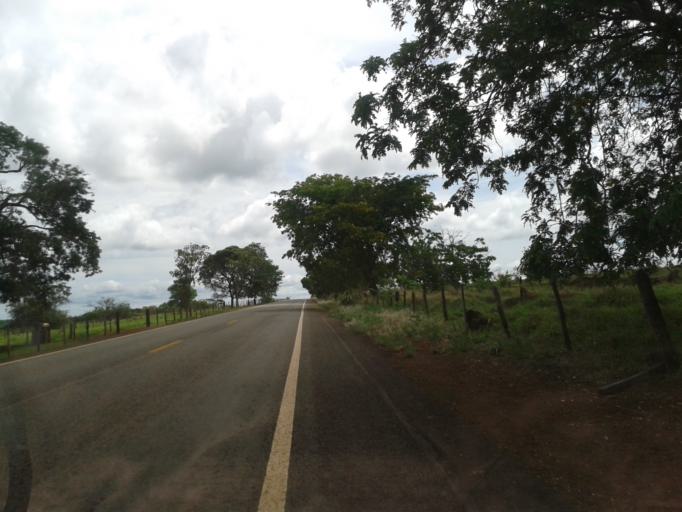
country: BR
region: Goias
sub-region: Buriti Alegre
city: Buriti Alegre
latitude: -18.1272
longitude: -49.1390
